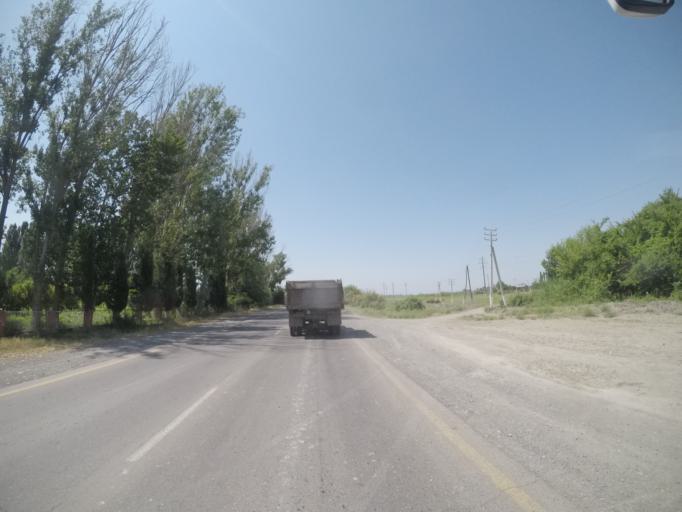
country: AZ
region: Agdas
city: Agdas
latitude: 40.5883
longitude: 47.4434
